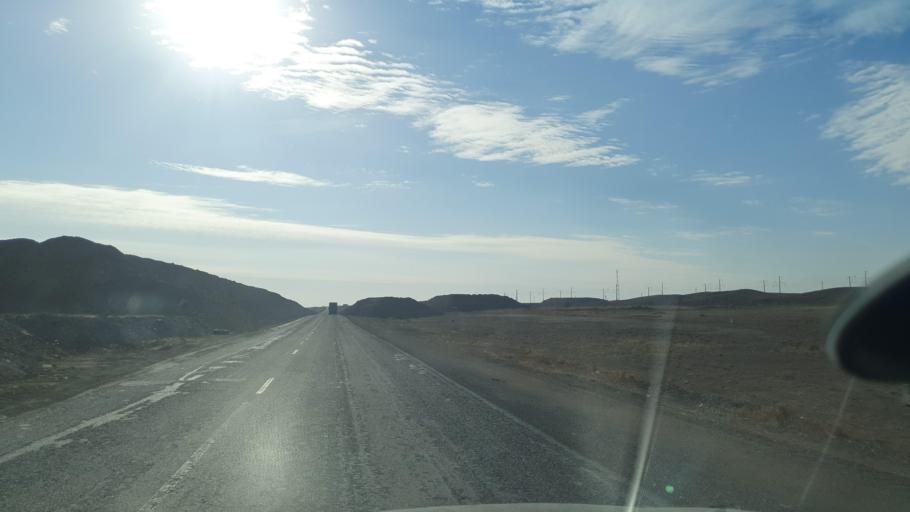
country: KZ
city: Priozersk
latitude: 45.8262
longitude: 73.4495
